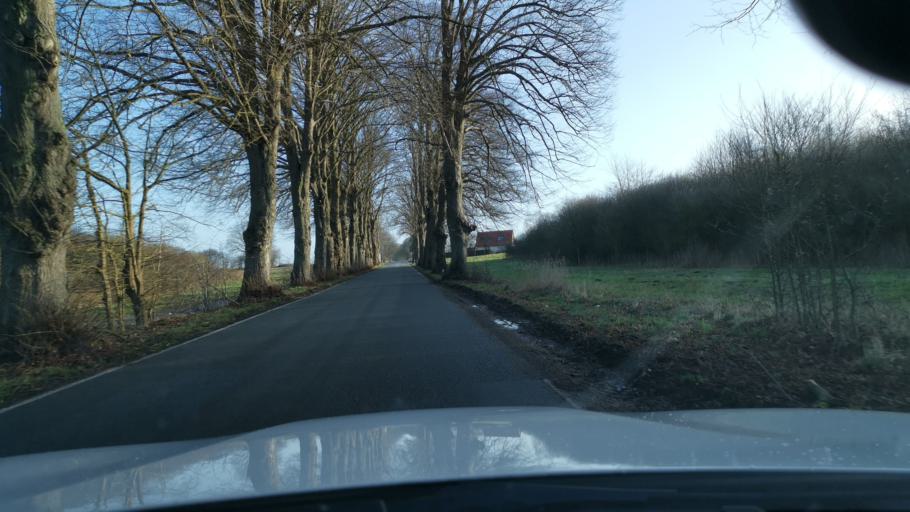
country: DE
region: Mecklenburg-Vorpommern
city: Wardow
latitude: 54.0021
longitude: 12.3882
